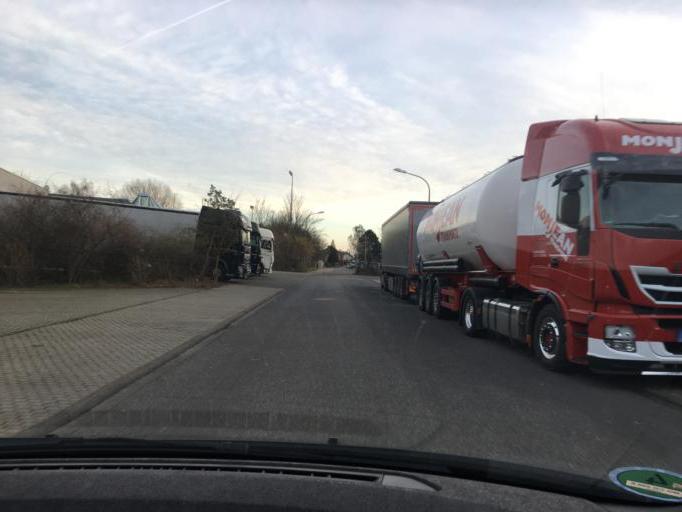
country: DE
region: North Rhine-Westphalia
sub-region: Regierungsbezirk Koln
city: Kreuzau
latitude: 50.7631
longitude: 6.5205
